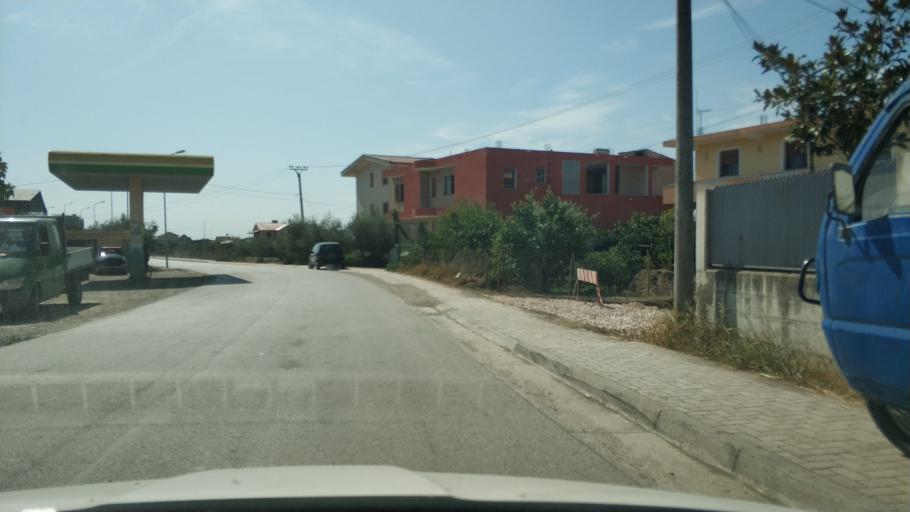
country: AL
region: Fier
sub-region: Rrethi i Lushnjes
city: Divjake
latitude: 40.9916
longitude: 19.5336
